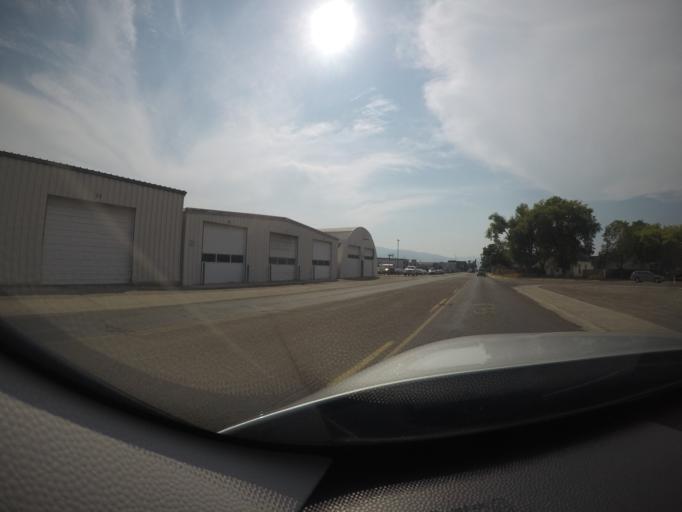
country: US
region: Montana
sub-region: Missoula County
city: Missoula
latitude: 46.8560
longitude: -114.0105
